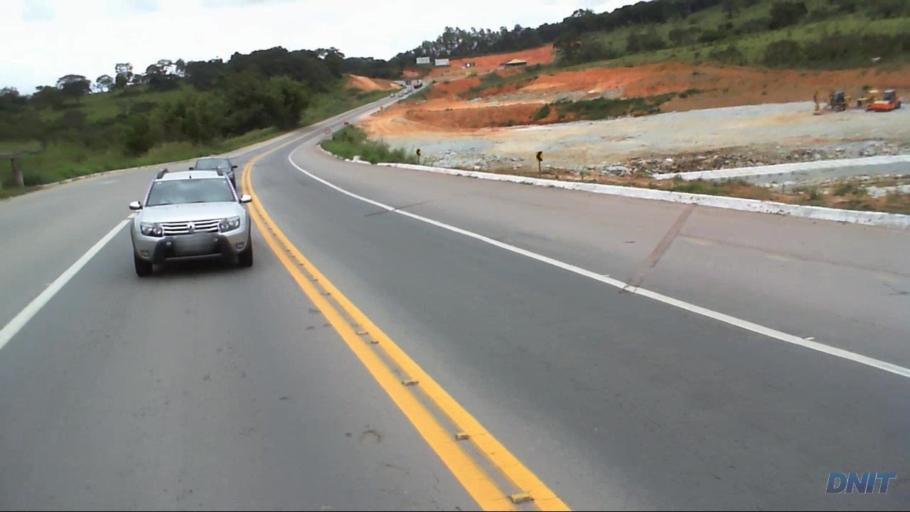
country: BR
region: Minas Gerais
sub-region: Barao De Cocais
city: Barao de Cocais
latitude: -19.7393
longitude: -43.5070
